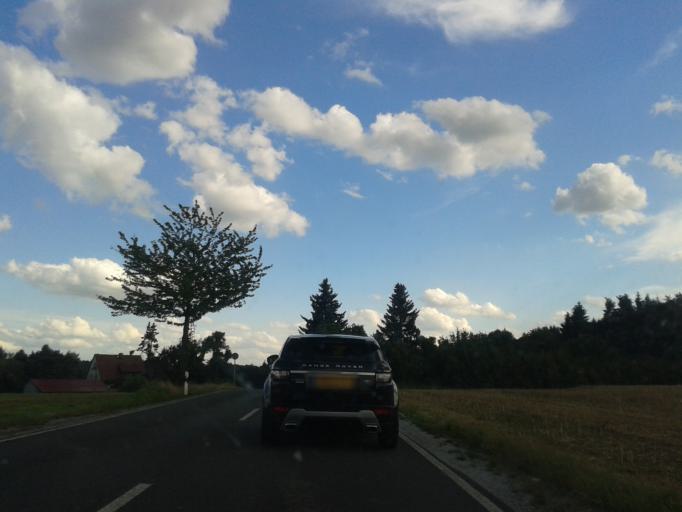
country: DE
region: Saxony
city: Radeberg
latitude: 51.0657
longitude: 13.9337
